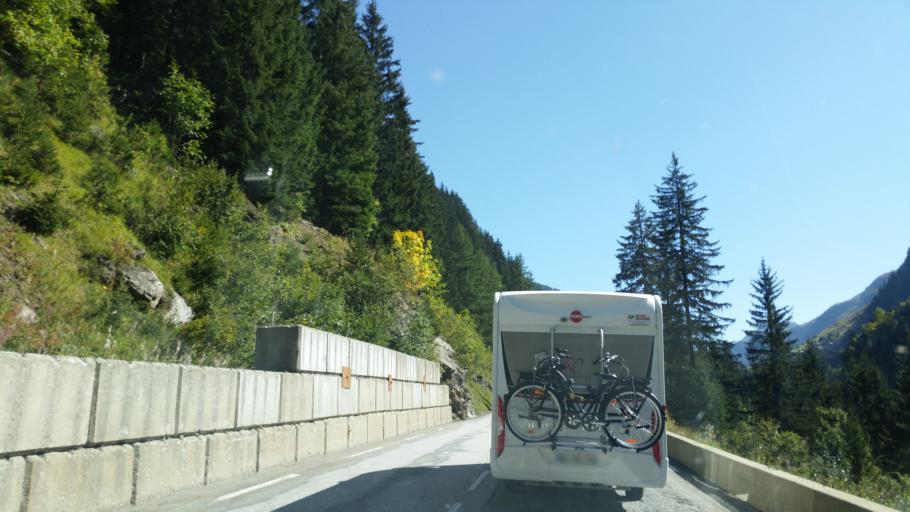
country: FR
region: Rhone-Alpes
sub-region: Departement de la Savoie
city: Tignes
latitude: 45.5485
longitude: 6.9065
